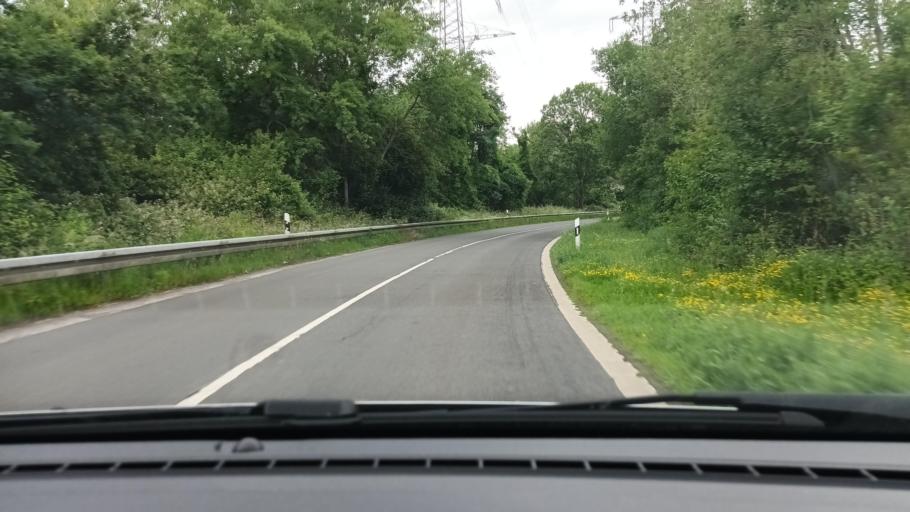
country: DE
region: North Rhine-Westphalia
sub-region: Regierungsbezirk Koln
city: Hurth
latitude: 50.8665
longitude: 6.8408
